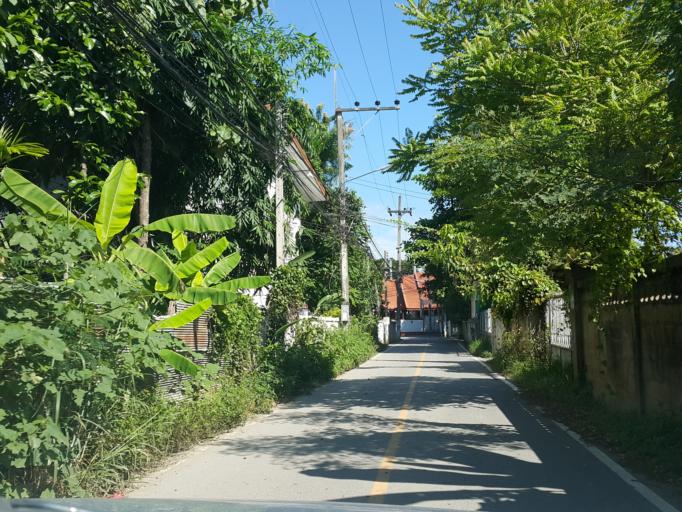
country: TH
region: Chiang Mai
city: San Sai
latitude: 18.8118
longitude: 99.0349
